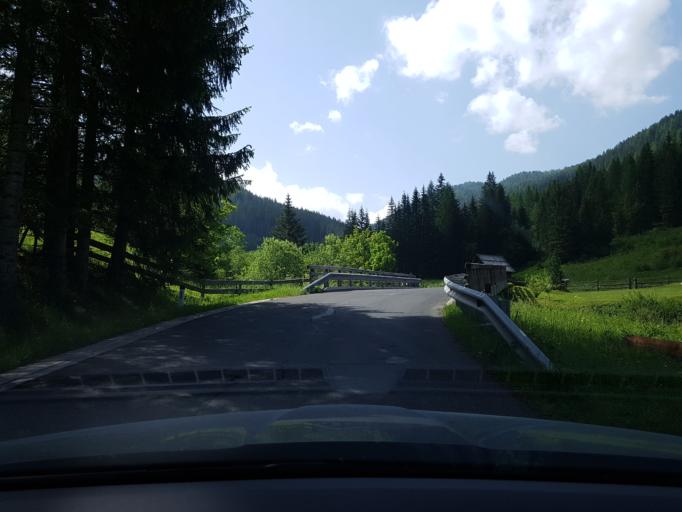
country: AT
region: Salzburg
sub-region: Politischer Bezirk Tamsweg
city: Thomatal
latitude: 47.0411
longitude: 13.7119
